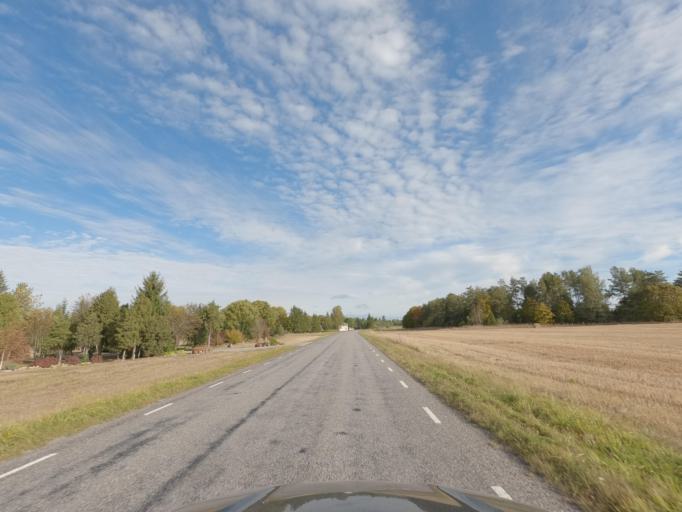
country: EE
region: Raplamaa
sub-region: Kohila vald
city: Kohila
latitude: 59.0967
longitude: 24.6734
